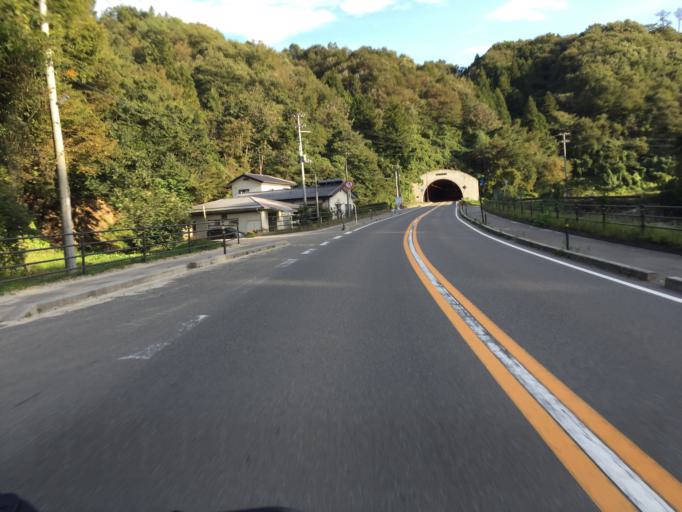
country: JP
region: Fukushima
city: Hobaramachi
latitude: 37.6897
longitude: 140.6160
